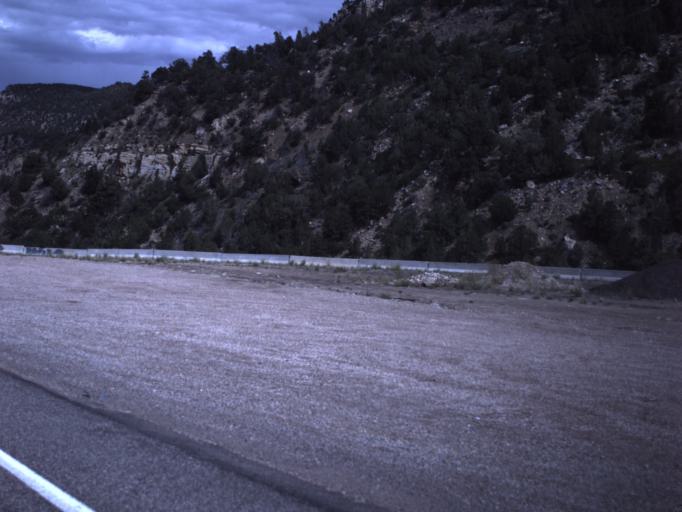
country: US
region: Utah
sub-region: Iron County
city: Cedar City
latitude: 37.6345
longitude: -112.9445
